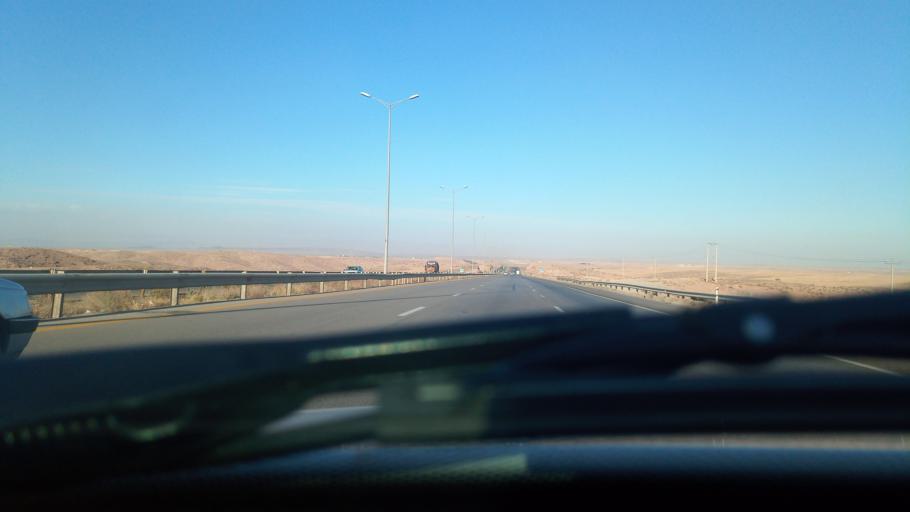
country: IR
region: Razavi Khorasan
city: Mashhad
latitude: 36.0468
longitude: 59.7022
